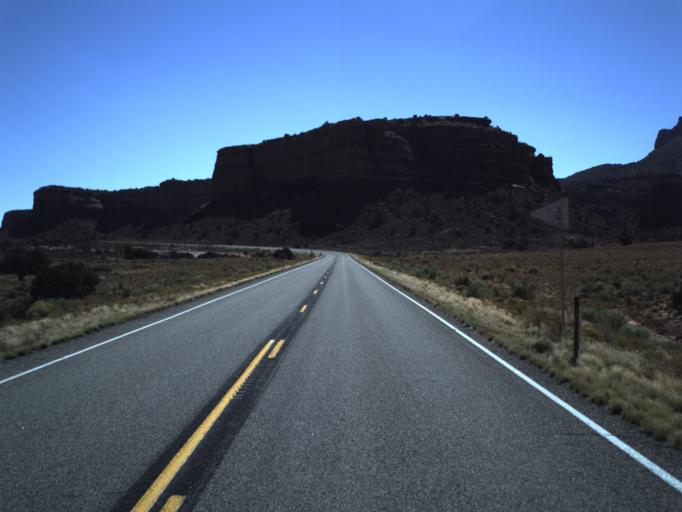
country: US
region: Utah
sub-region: San Juan County
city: Blanding
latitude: 37.7396
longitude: -110.2754
